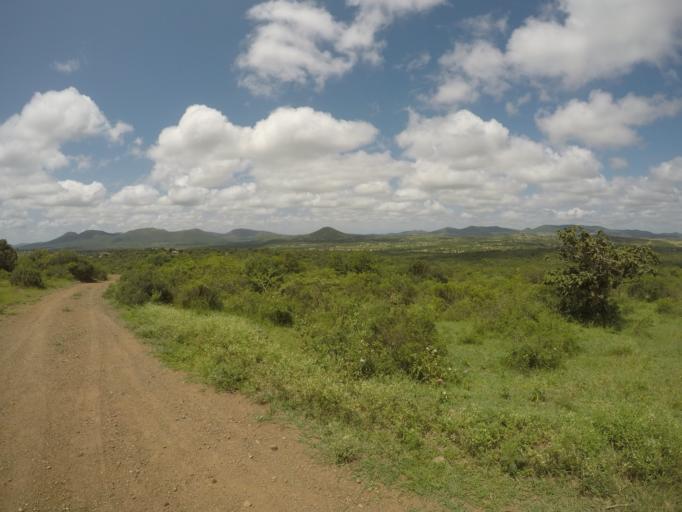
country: ZA
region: KwaZulu-Natal
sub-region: uThungulu District Municipality
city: Empangeni
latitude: -28.5854
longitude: 31.8260
